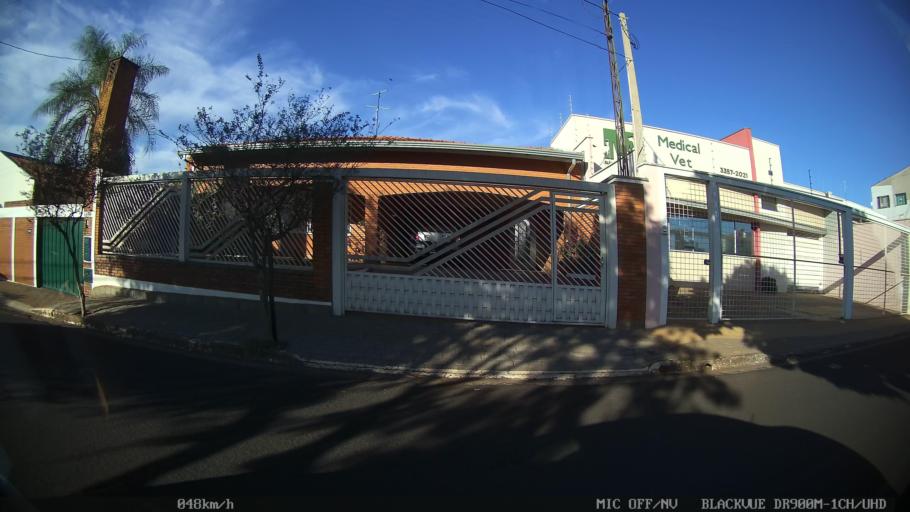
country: BR
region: Sao Paulo
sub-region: Araraquara
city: Araraquara
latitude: -21.7547
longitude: -48.1629
